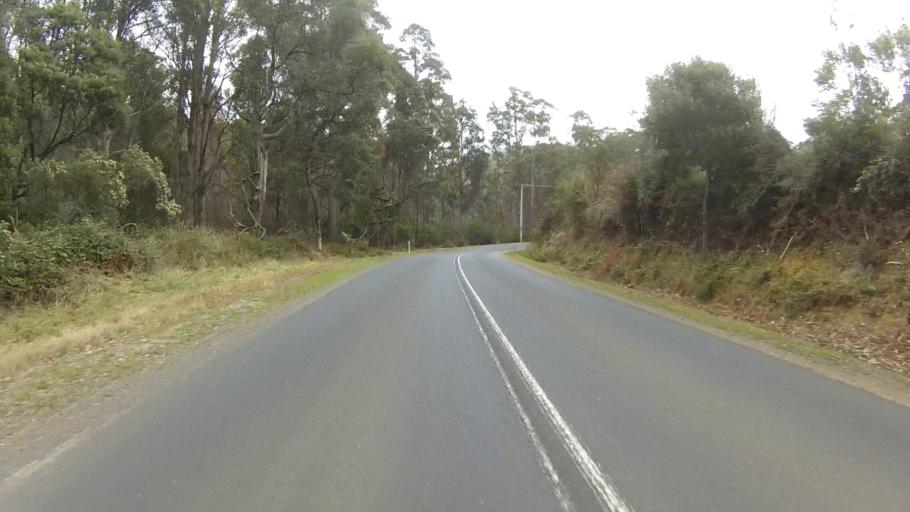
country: AU
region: Tasmania
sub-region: Huon Valley
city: Cygnet
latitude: -43.1400
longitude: 147.1524
